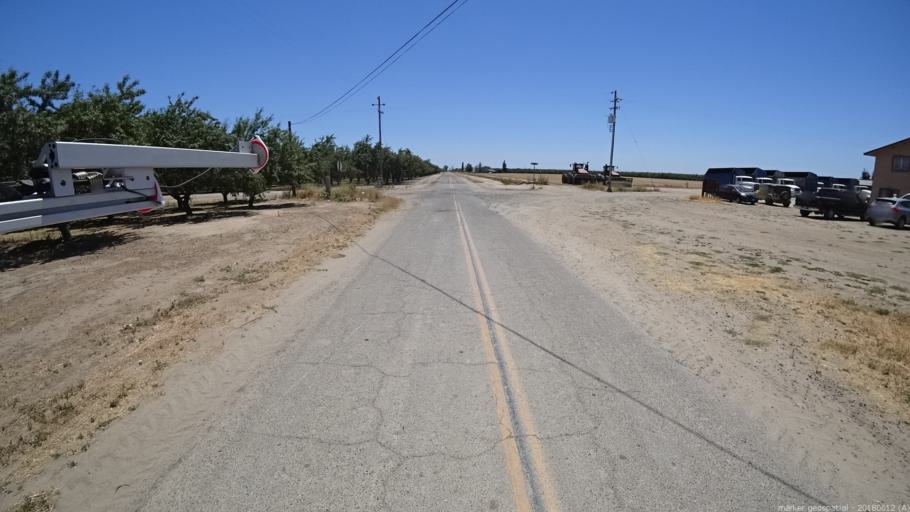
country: US
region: California
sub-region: Madera County
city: Chowchilla
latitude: 37.0694
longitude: -120.2659
